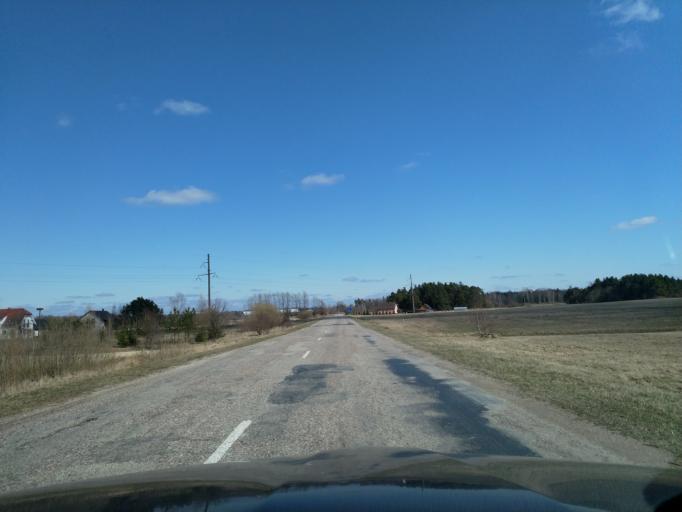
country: LV
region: Kuldigas Rajons
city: Kuldiga
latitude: 56.9722
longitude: 22.0023
